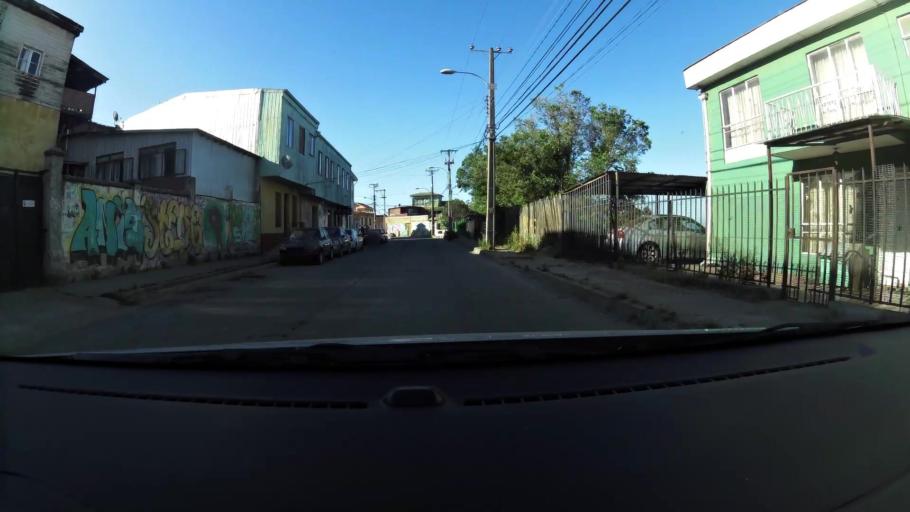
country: CL
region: Valparaiso
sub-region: Provincia de Valparaiso
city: Valparaiso
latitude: -33.0537
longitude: -71.6245
